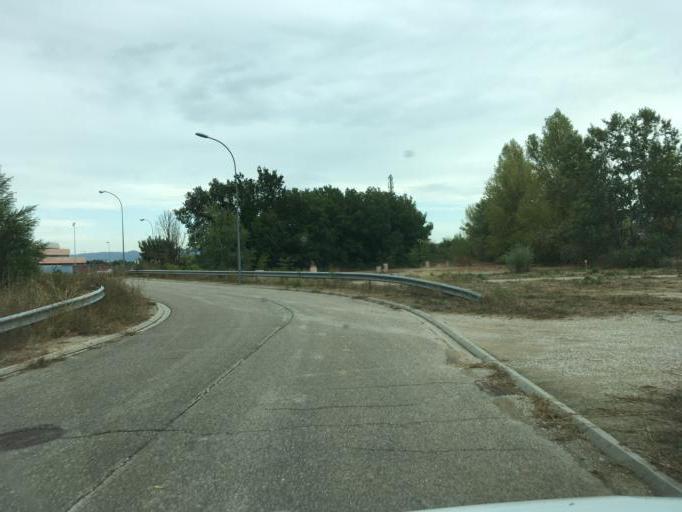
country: FR
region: Provence-Alpes-Cote d'Azur
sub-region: Departement des Bouches-du-Rhone
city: Rousset
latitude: 43.4749
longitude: 5.6004
